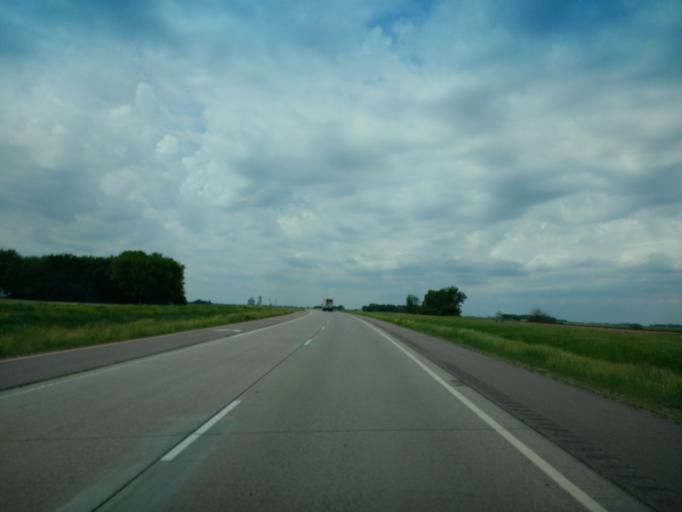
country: US
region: Minnesota
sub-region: Cottonwood County
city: Mountain Lake
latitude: 43.9495
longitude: -94.8438
